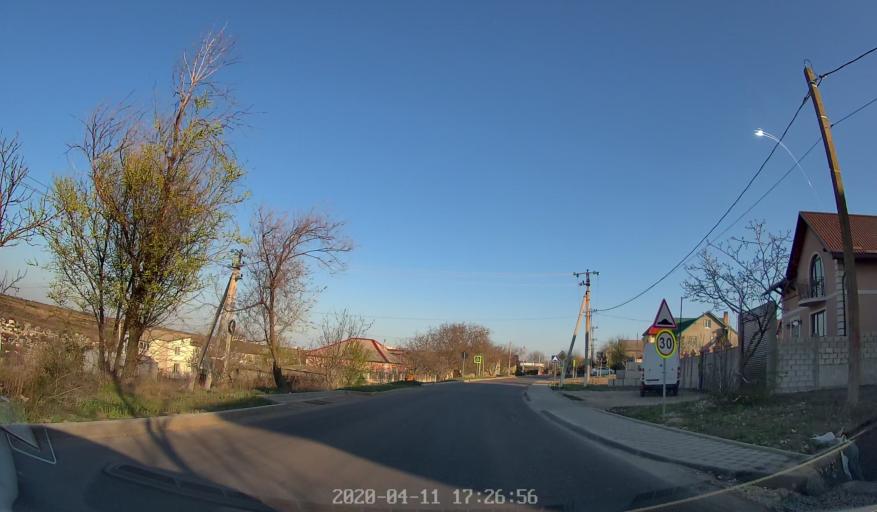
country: MD
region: Chisinau
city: Vatra
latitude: 47.0115
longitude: 28.7599
